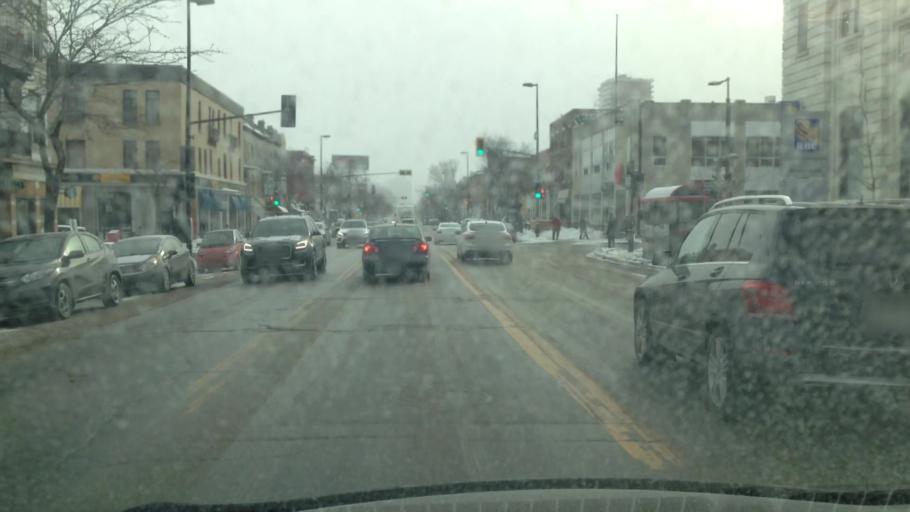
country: CA
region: Quebec
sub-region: Montreal
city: Montreal
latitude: 45.5199
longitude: -73.5964
